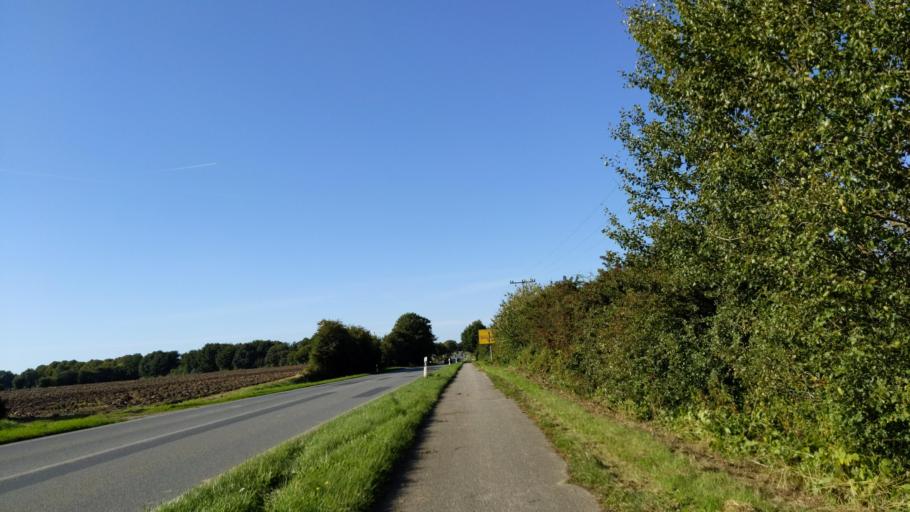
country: DE
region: Schleswig-Holstein
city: Ahrensbok
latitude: 53.9603
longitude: 10.6104
